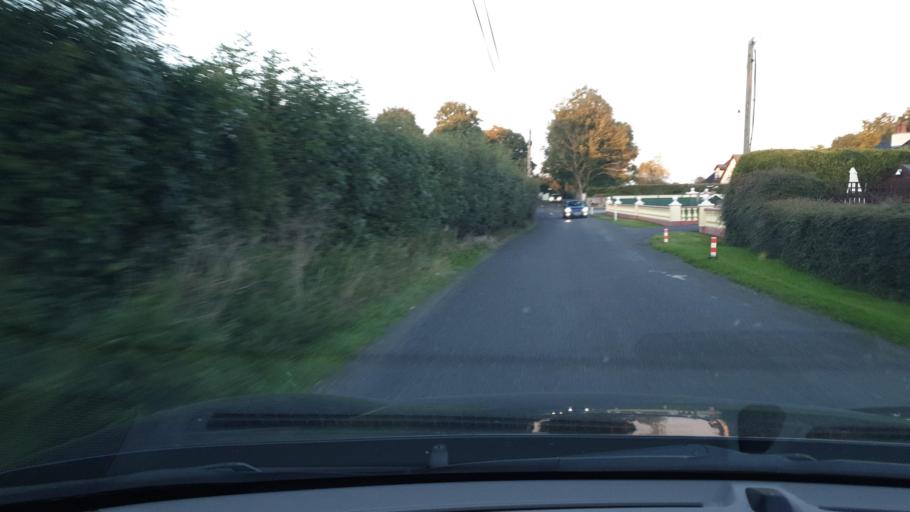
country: IE
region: Leinster
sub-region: Kildare
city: Prosperous
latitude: 53.3160
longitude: -6.8205
